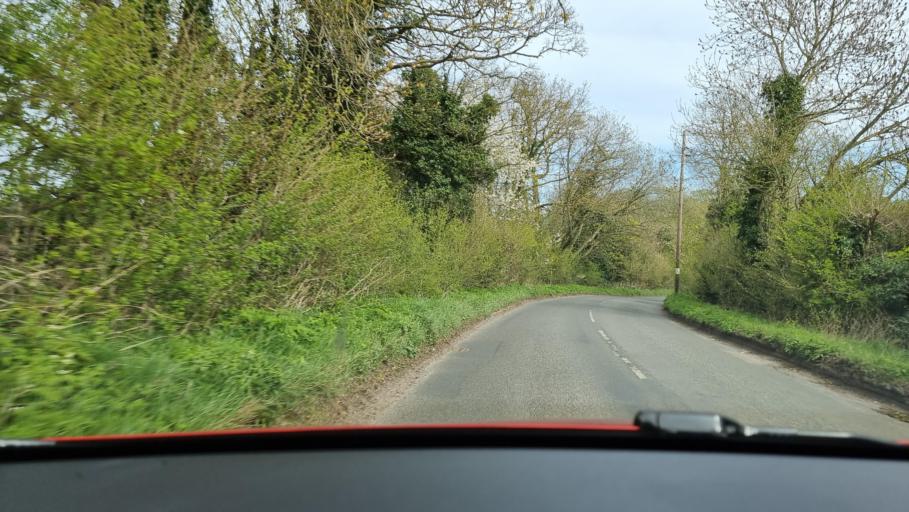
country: GB
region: England
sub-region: Oxfordshire
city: Oxford
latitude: 51.8072
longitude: -1.2212
